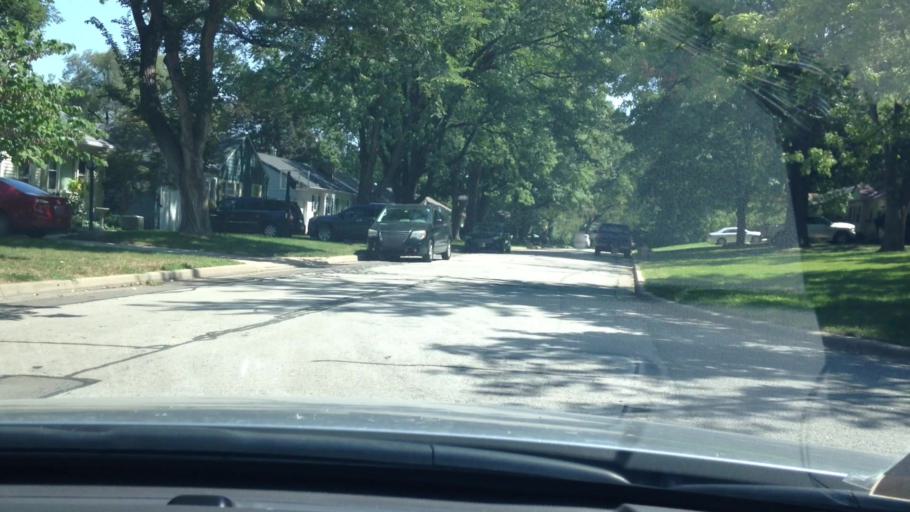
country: US
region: Kansas
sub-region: Johnson County
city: Roeland Park
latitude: 39.0327
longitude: -94.6426
